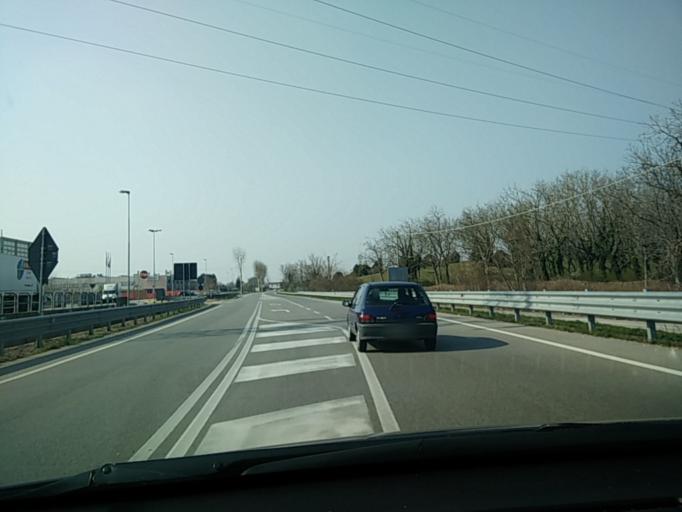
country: IT
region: Veneto
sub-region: Provincia di Treviso
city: Castagnole
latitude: 45.7043
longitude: 12.1752
